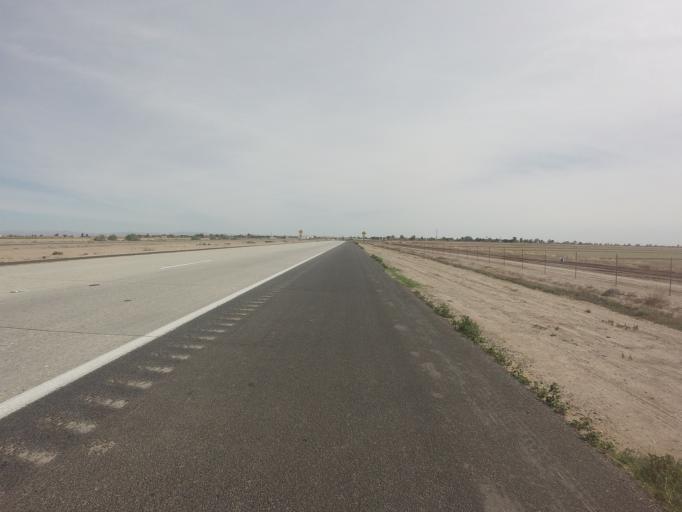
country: US
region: California
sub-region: Imperial County
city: Westmorland
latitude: 33.0370
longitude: -115.6409
